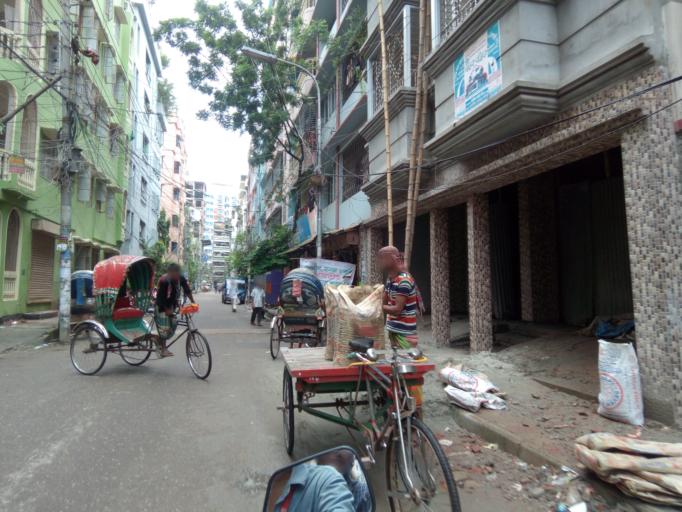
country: BD
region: Dhaka
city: Azimpur
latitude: 23.7599
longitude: 90.3625
